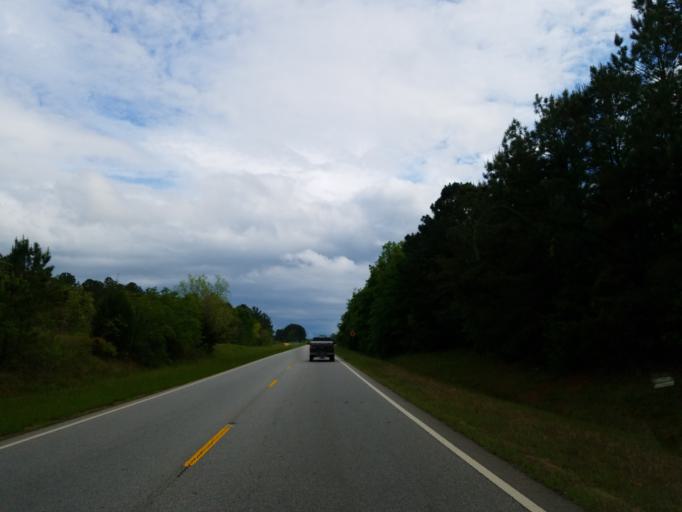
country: US
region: Georgia
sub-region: Crawford County
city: Roberta
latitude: 32.8148
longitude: -84.0531
